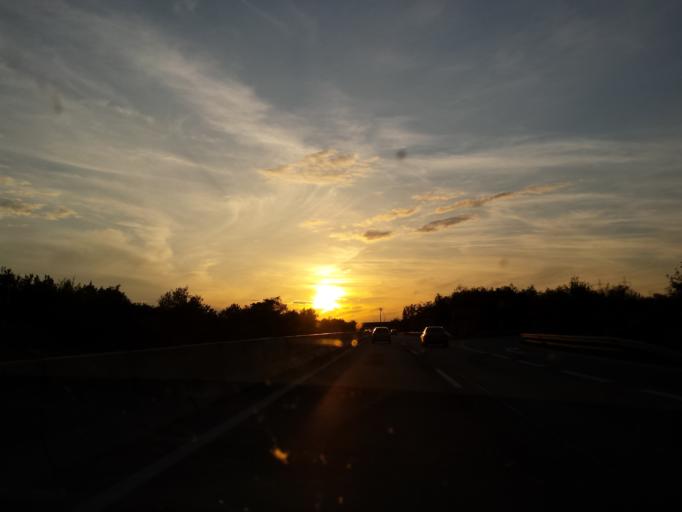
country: AT
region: Burgenland
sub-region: Politischer Bezirk Neusiedl am See
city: Bruckneudorf
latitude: 48.0348
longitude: 16.8180
